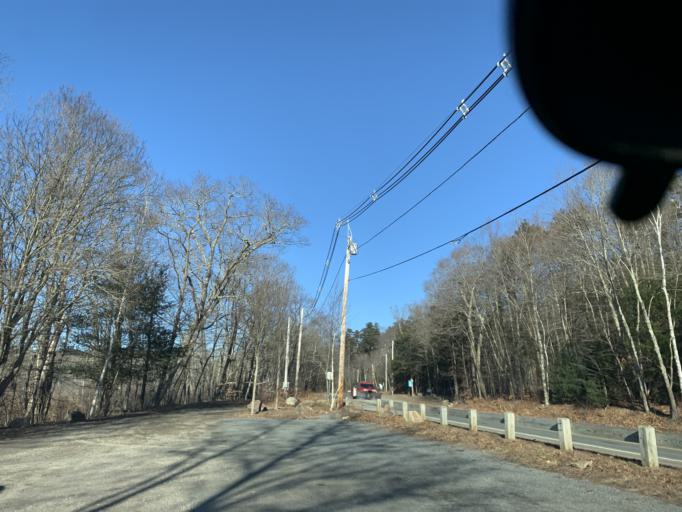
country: US
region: Massachusetts
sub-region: Essex County
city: Essex
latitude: 42.5973
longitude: -70.7676
